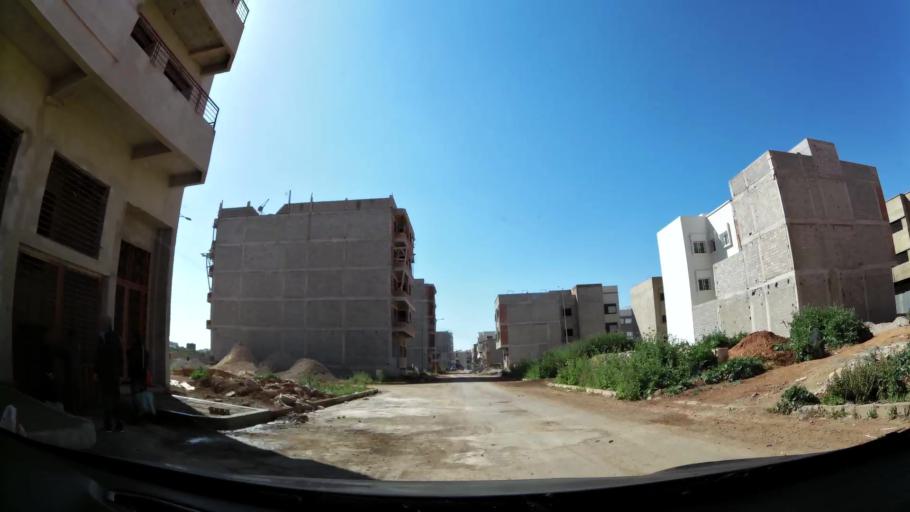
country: MA
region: Fes-Boulemane
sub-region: Fes
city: Fes
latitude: 33.9928
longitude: -5.0087
